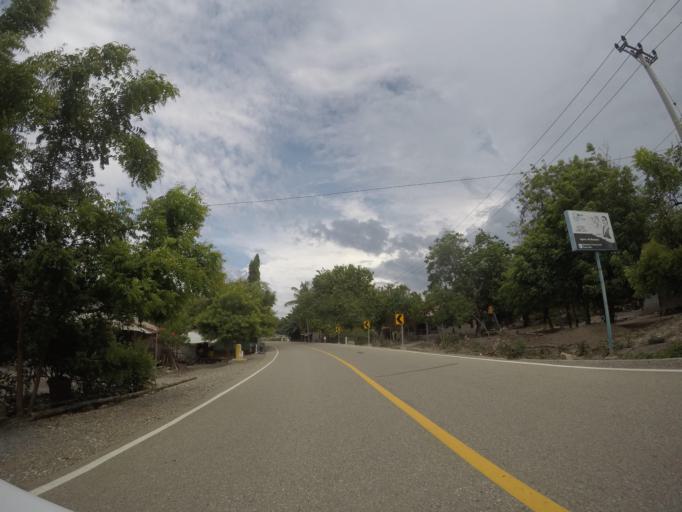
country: TL
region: Liquica
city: Maubara
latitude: -8.6118
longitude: 125.2015
